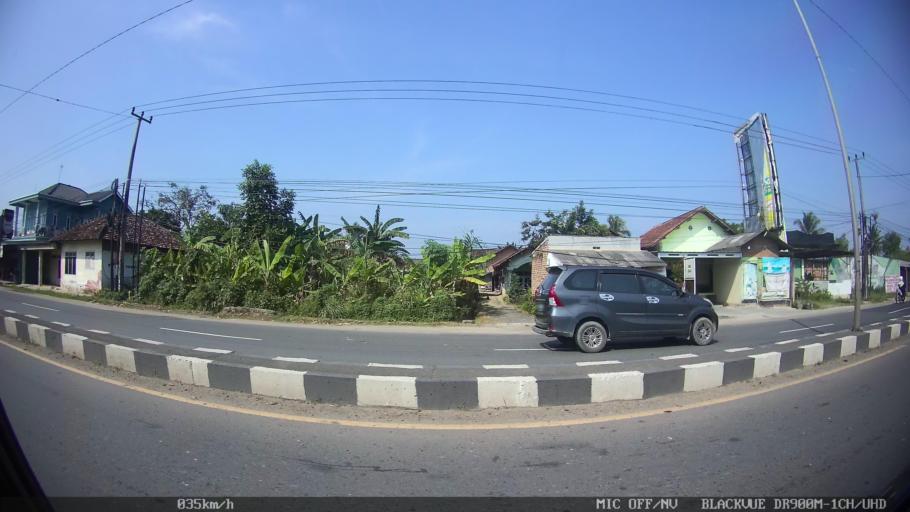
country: ID
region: Lampung
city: Natar
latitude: -5.2493
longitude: 105.1809
